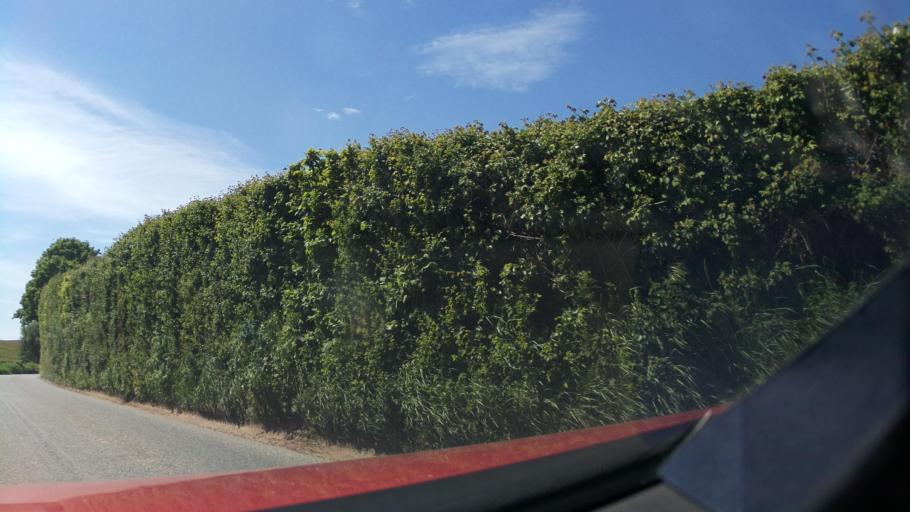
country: GB
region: England
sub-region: Devon
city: Ottery St Mary
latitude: 50.7662
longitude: -3.2646
